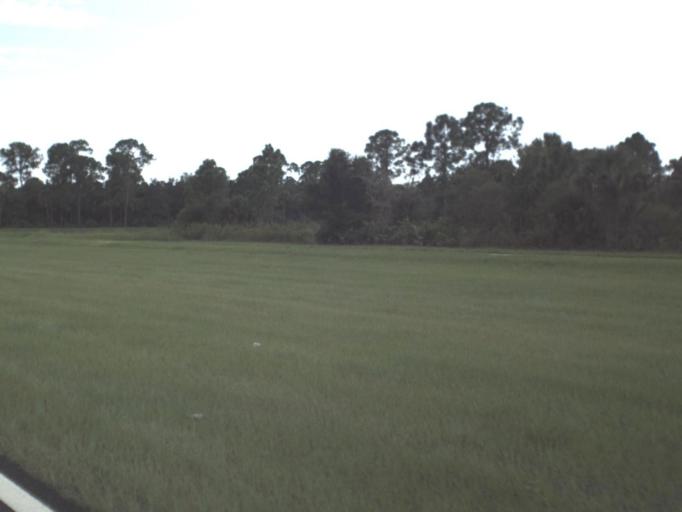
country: US
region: Florida
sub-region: Sarasota County
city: Warm Mineral Springs
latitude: 27.0487
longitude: -82.3059
